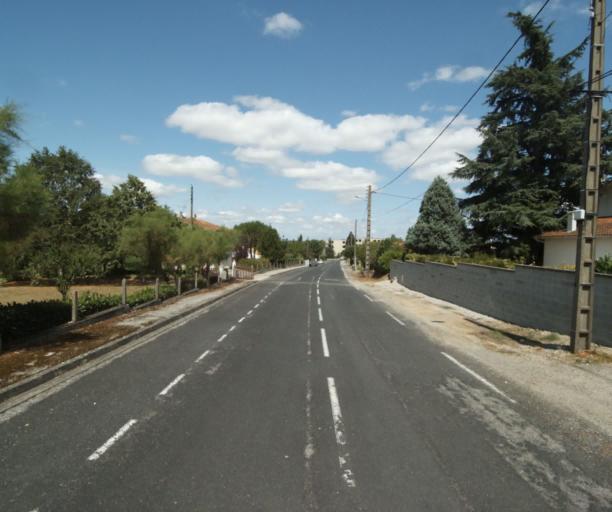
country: FR
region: Midi-Pyrenees
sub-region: Departement de la Haute-Garonne
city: Revel
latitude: 43.4492
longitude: 2.0091
